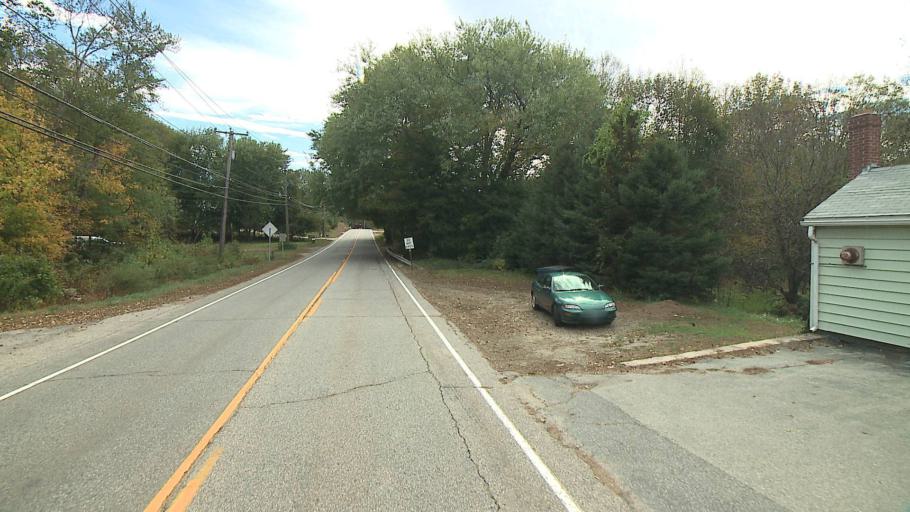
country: US
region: Connecticut
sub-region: Windham County
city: Killingly Center
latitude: 41.8595
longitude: -71.8819
